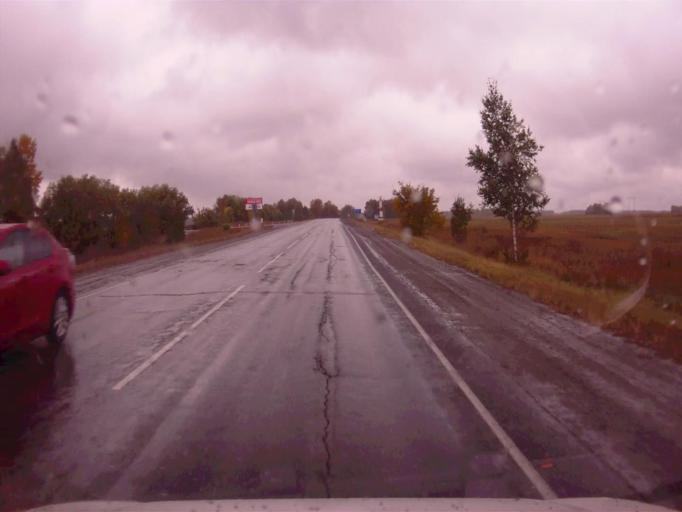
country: RU
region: Chelyabinsk
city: Roshchino
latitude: 55.3937
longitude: 61.1086
